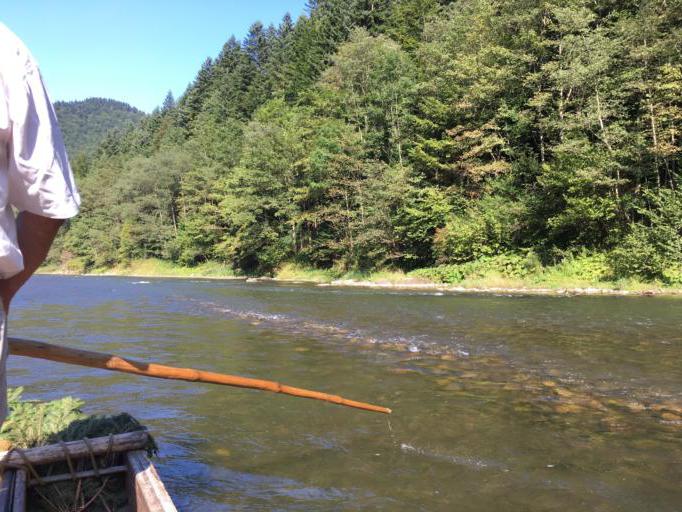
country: PL
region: Lesser Poland Voivodeship
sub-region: Powiat nowotarski
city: Kroscienko nad Dunajcem
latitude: 49.3970
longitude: 20.4337
